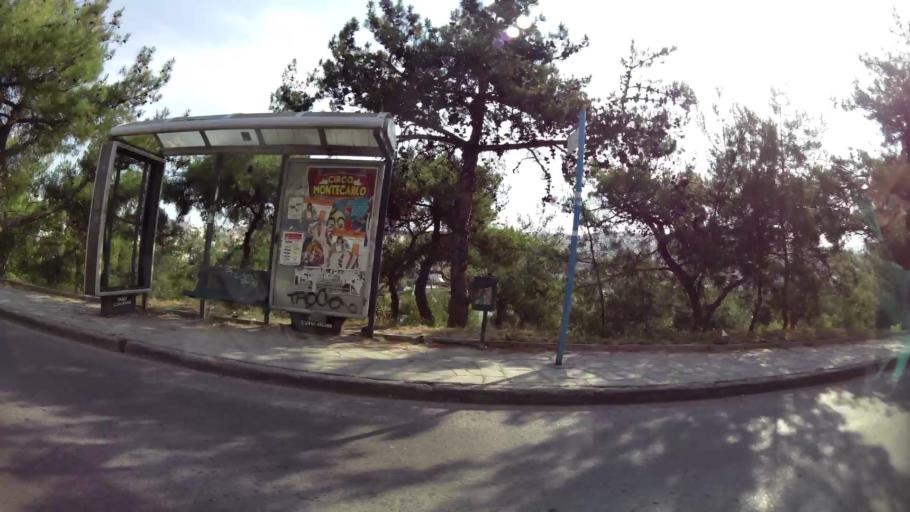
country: GR
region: Central Macedonia
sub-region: Nomos Thessalonikis
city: Sykies
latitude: 40.6576
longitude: 22.9502
